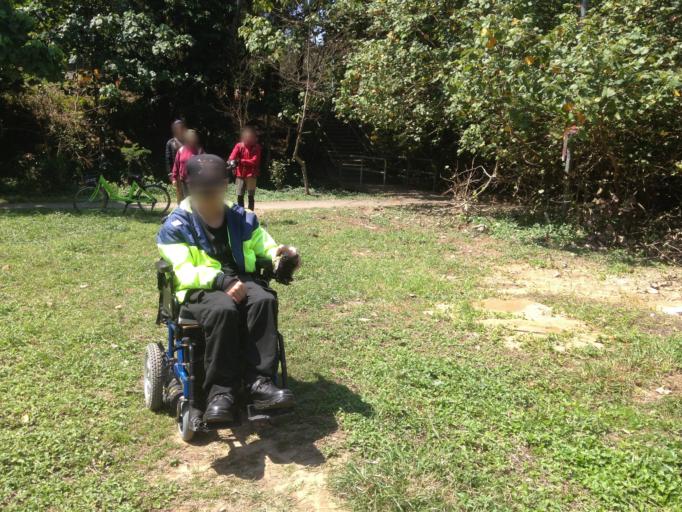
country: HK
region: Sai Kung
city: Sai Kung
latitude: 22.4306
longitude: 114.2563
